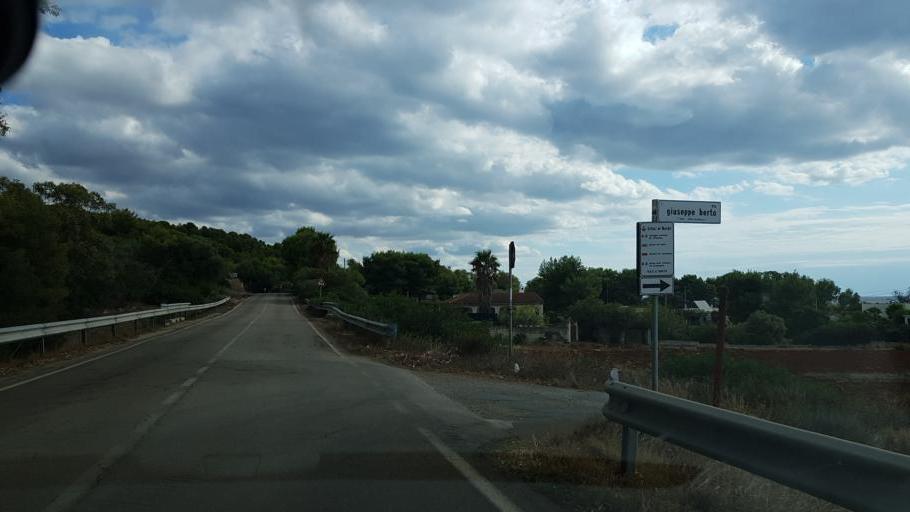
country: IT
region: Apulia
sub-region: Provincia di Lecce
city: Nardo
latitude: 40.1692
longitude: 17.9494
